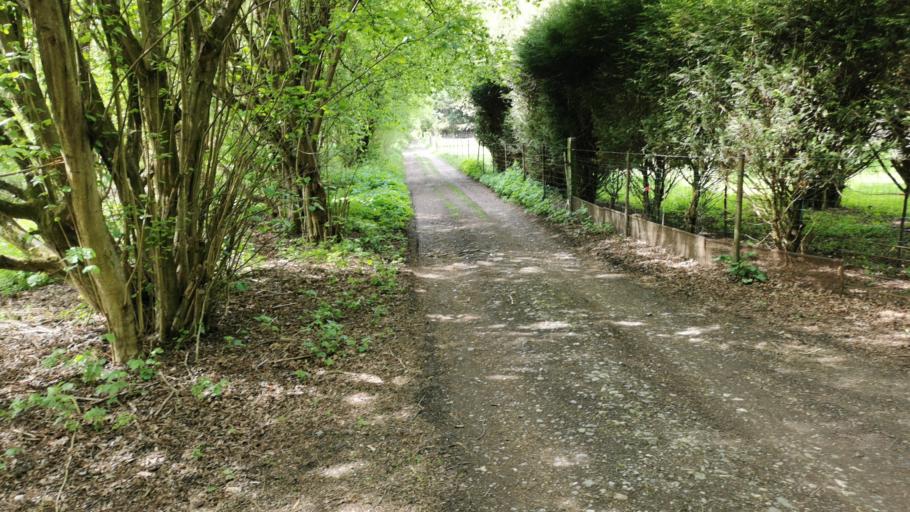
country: FR
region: Picardie
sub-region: Departement de la Somme
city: Doingt
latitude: 49.9182
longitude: 3.0122
